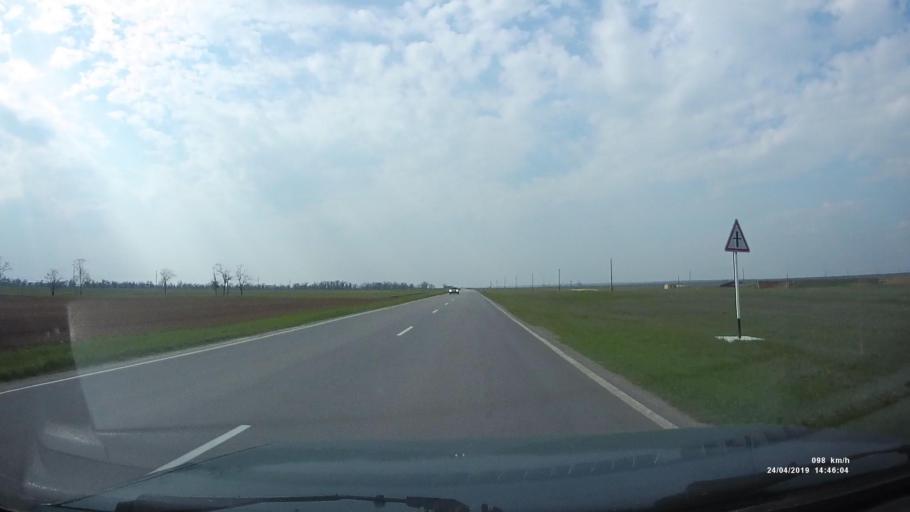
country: RU
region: Rostov
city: Remontnoye
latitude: 46.4786
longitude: 43.7962
